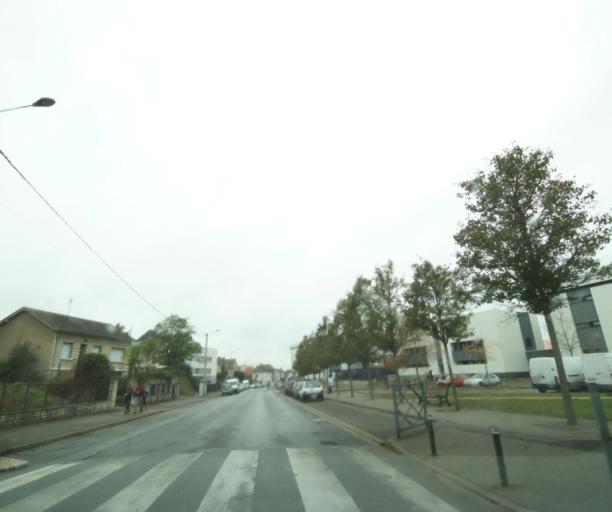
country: FR
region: Centre
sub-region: Departement d'Eure-et-Loir
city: Dreux
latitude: 48.7304
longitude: 1.3792
